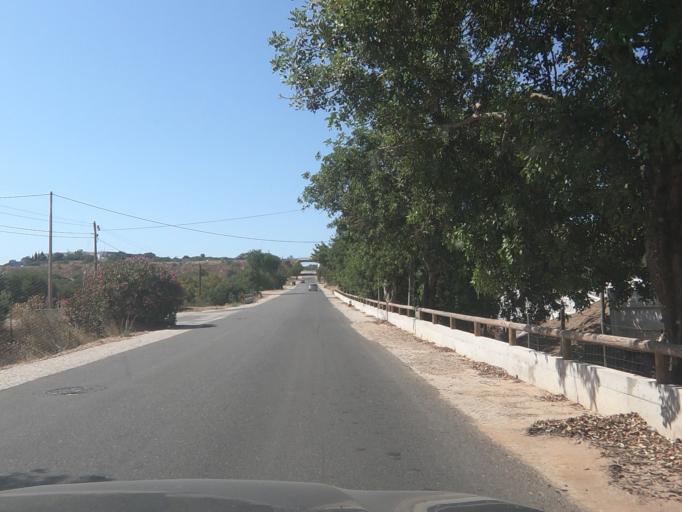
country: PT
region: Faro
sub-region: Faro
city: Santa Barbara de Nexe
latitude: 37.0897
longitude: -7.9932
